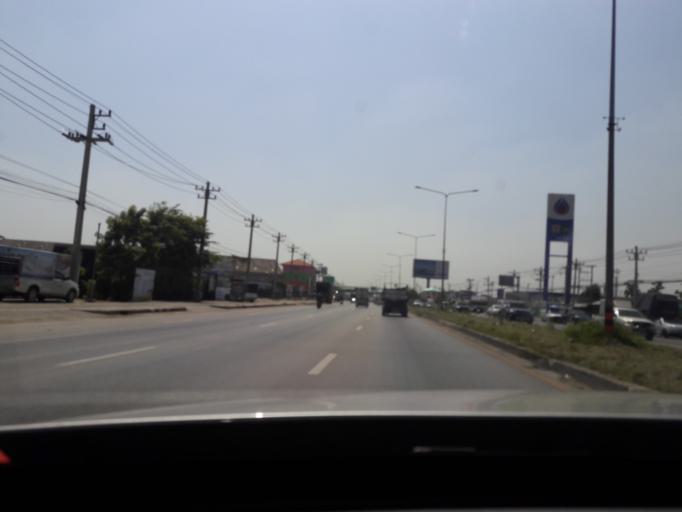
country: TH
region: Bangkok
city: Nong Khaem
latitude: 13.6784
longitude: 100.3202
